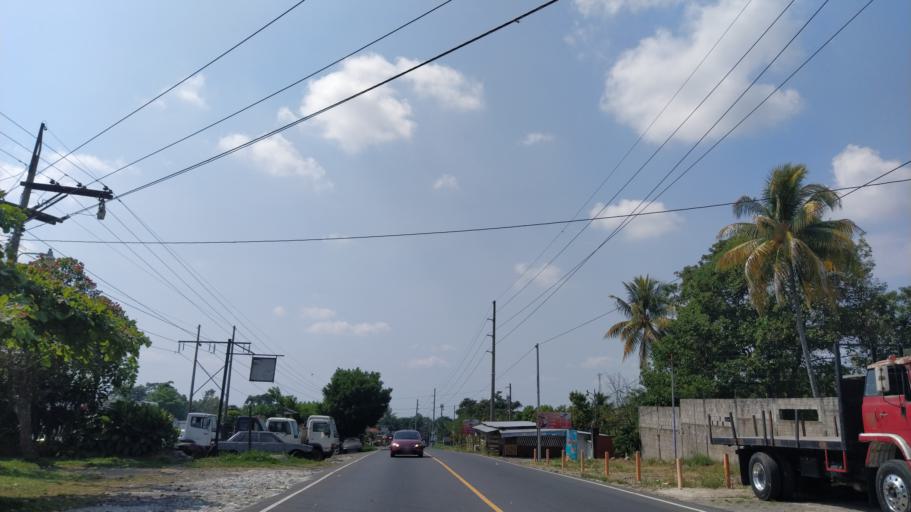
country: GT
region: Retalhuleu
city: San Felipe
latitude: 14.6207
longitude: -91.5904
